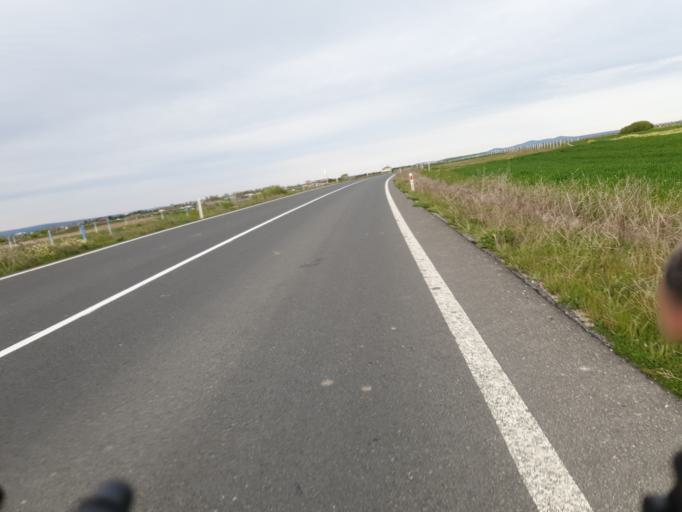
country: TR
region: Tekirdag
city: Saray
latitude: 41.3857
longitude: 27.8848
